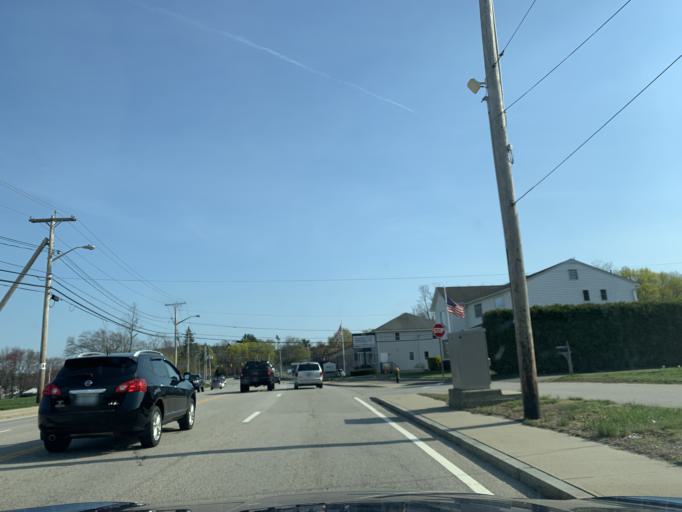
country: US
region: Rhode Island
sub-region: Providence County
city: Johnston
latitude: 41.8106
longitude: -71.4949
